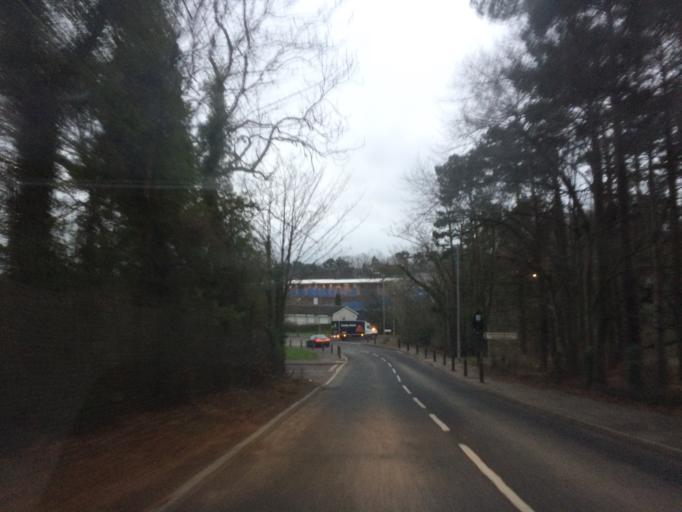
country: GB
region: Scotland
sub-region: East Renfrewshire
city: Newton Mearns
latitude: 55.7875
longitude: -4.3306
